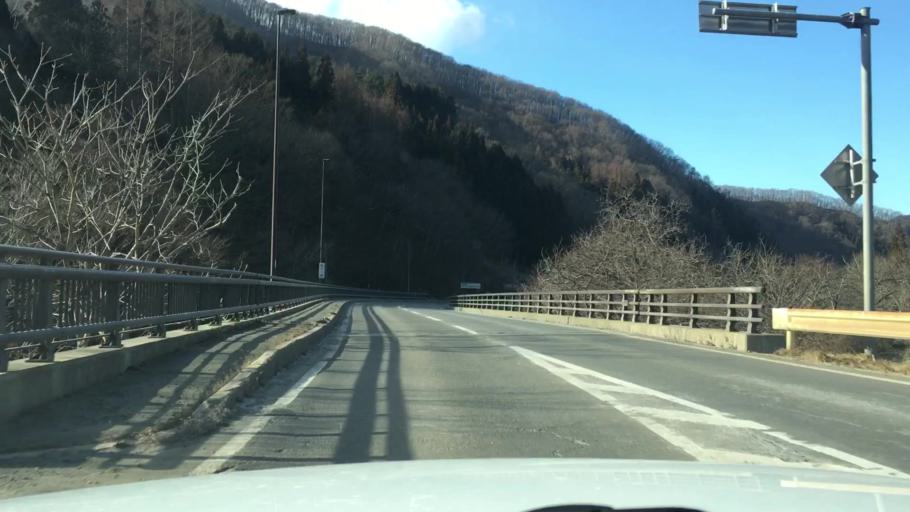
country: JP
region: Iwate
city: Tono
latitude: 39.6151
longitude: 141.6267
